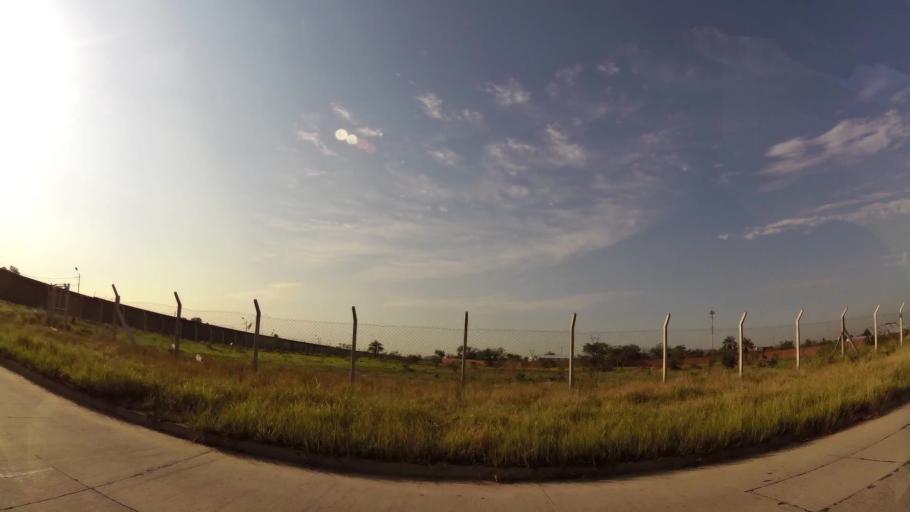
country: BO
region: Santa Cruz
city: Santa Cruz de la Sierra
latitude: -17.6822
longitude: -63.1492
